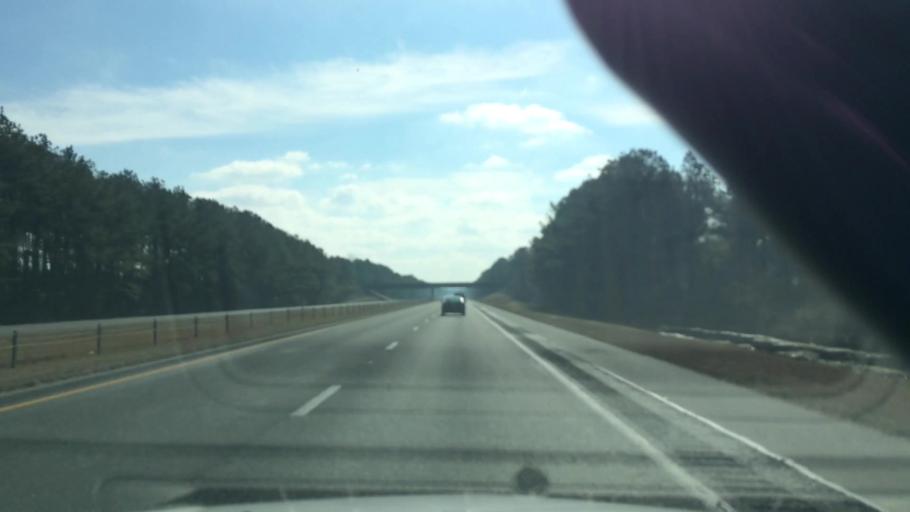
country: US
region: North Carolina
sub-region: Duplin County
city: Wallace
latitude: 34.7353
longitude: -77.9448
